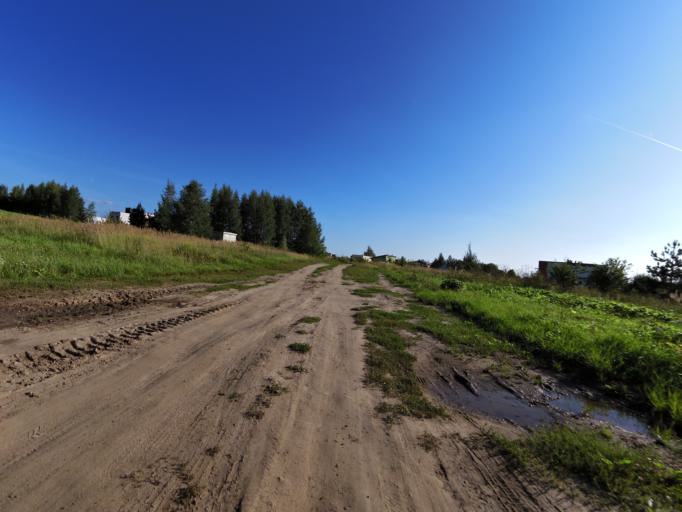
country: LT
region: Vilnius County
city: Pilaite
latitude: 54.7202
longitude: 25.1817
